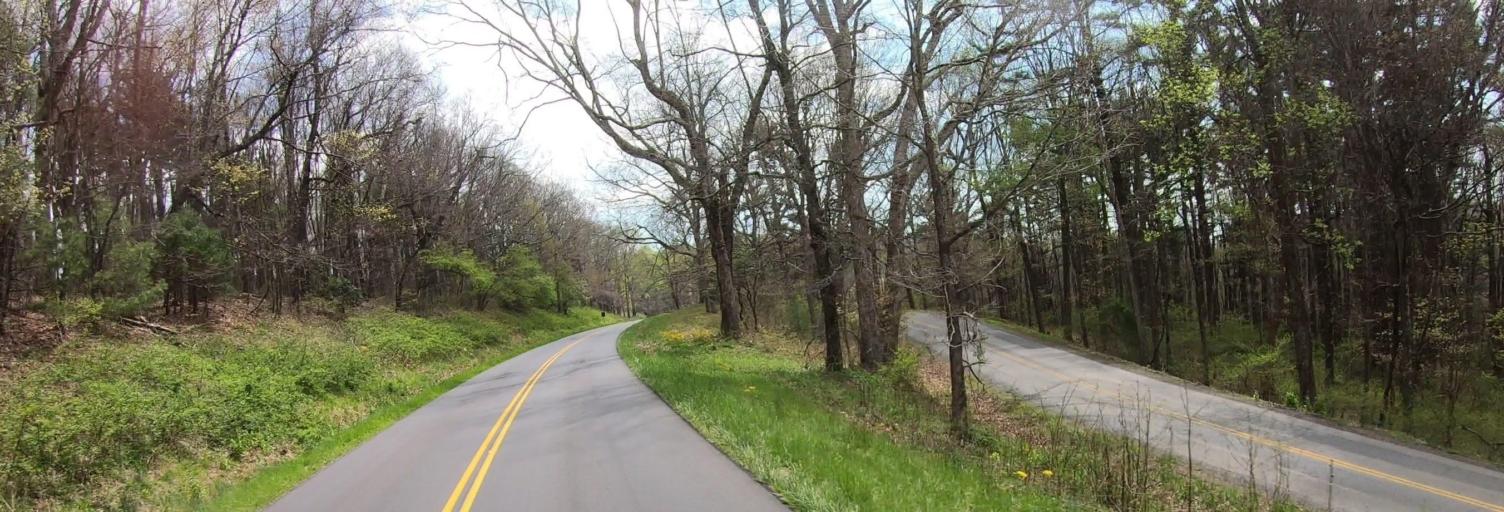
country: US
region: Virginia
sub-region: Carroll County
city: Cana
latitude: 36.6685
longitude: -80.6833
